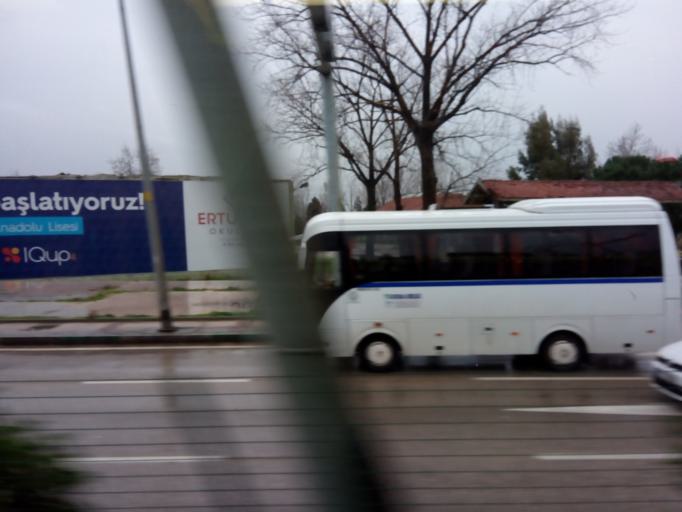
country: TR
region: Bursa
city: Yildirim
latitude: 40.2113
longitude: 29.0229
